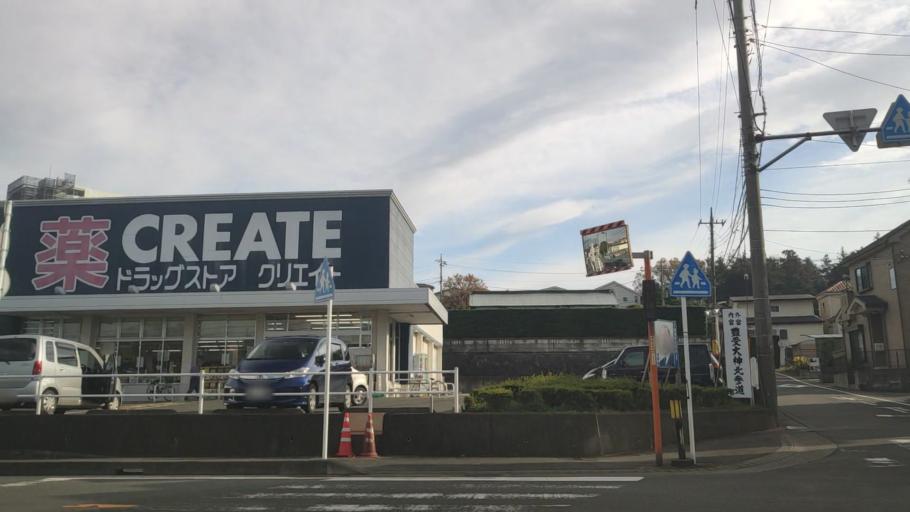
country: JP
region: Kanagawa
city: Atsugi
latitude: 35.4278
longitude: 139.3980
